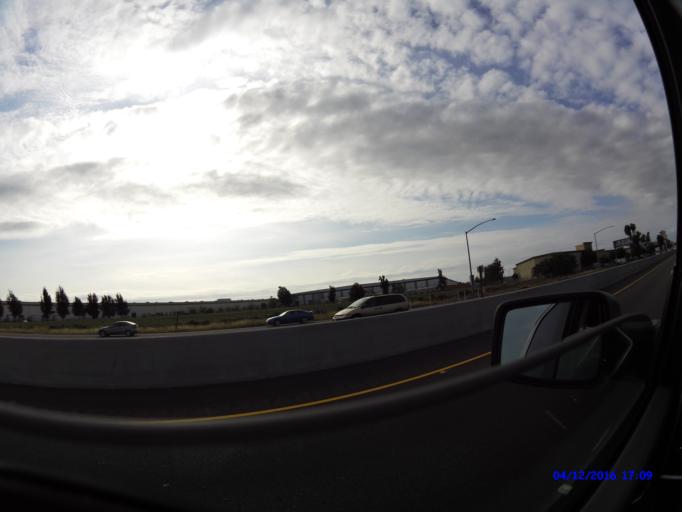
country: US
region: California
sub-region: San Joaquin County
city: Manteca
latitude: 37.7897
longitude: -121.1891
